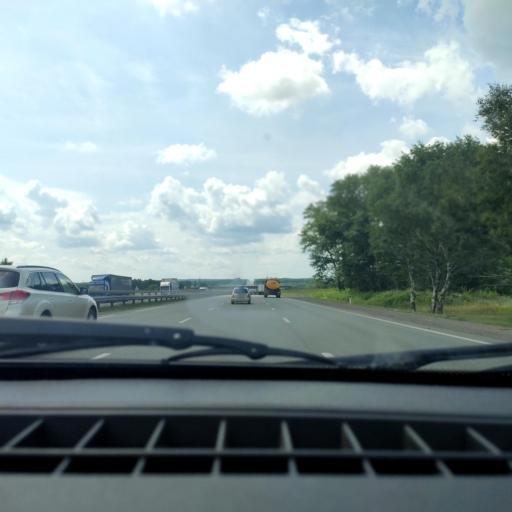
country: RU
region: Bashkortostan
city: Avdon
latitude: 54.6679
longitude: 55.7597
